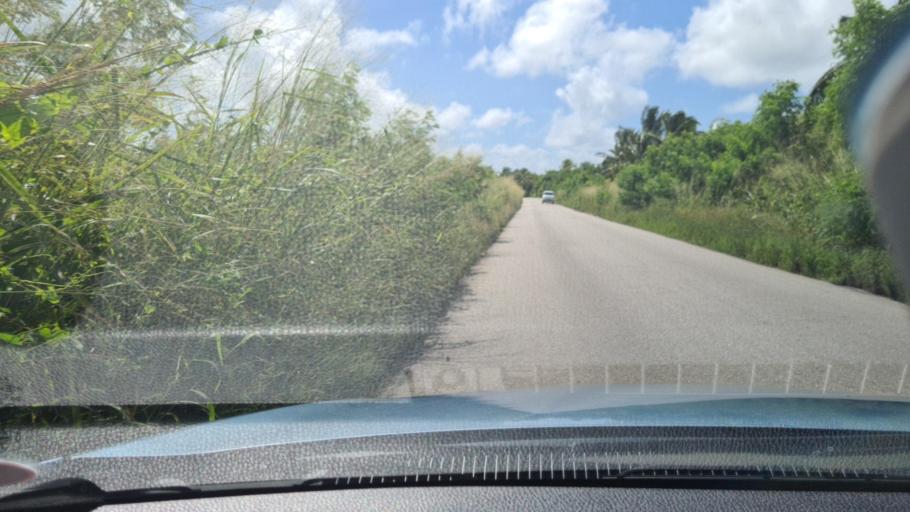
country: BB
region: Christ Church
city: Oistins
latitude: 13.0922
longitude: -59.5204
